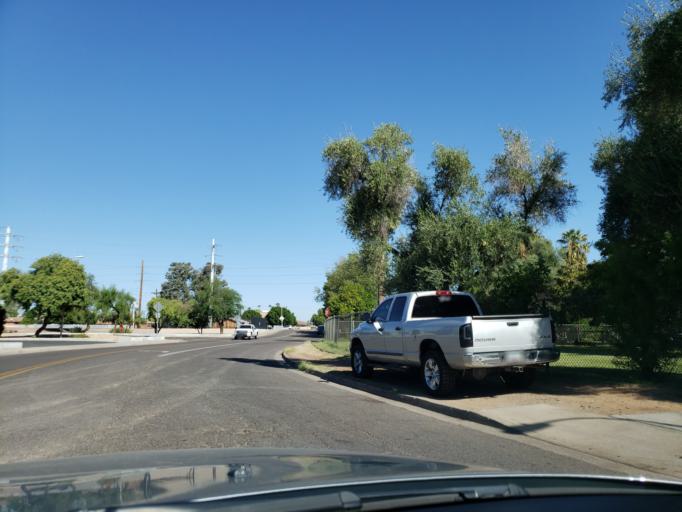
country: US
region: Arizona
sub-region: Maricopa County
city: Glendale
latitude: 33.4872
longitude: -112.1601
